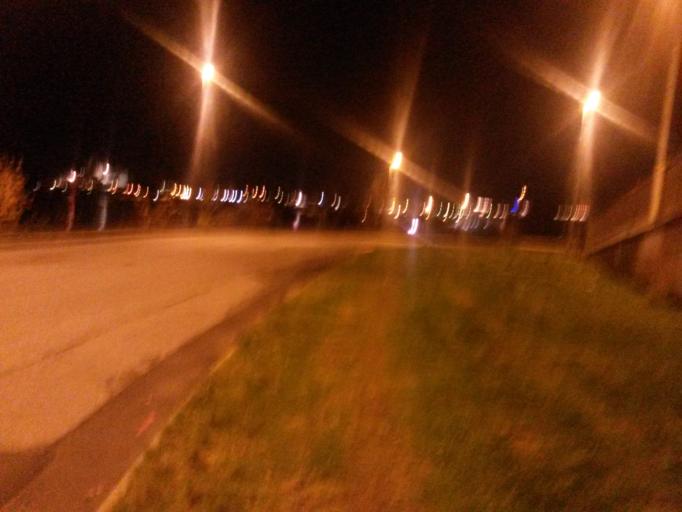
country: NO
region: Rogaland
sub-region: Stavanger
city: Stavanger
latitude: 58.9551
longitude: 5.7459
